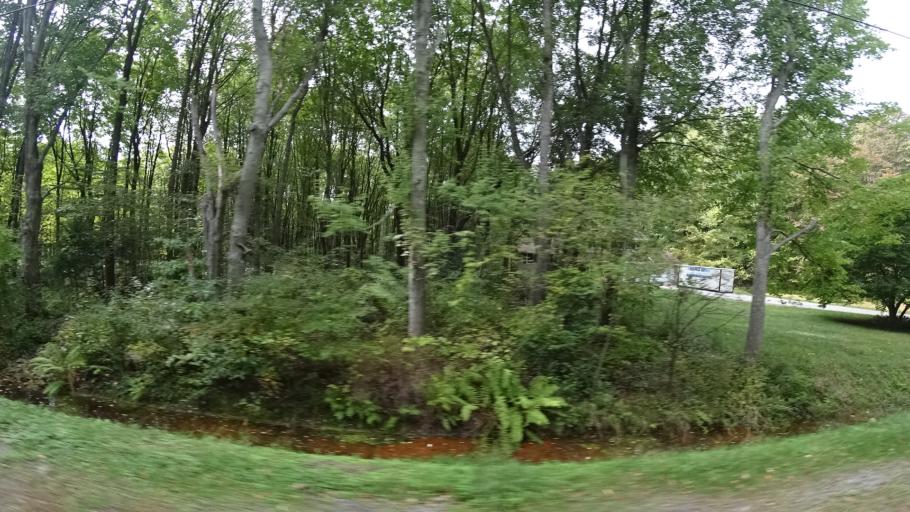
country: US
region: Indiana
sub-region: LaPorte County
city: Long Beach
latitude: 41.7373
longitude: -86.8362
